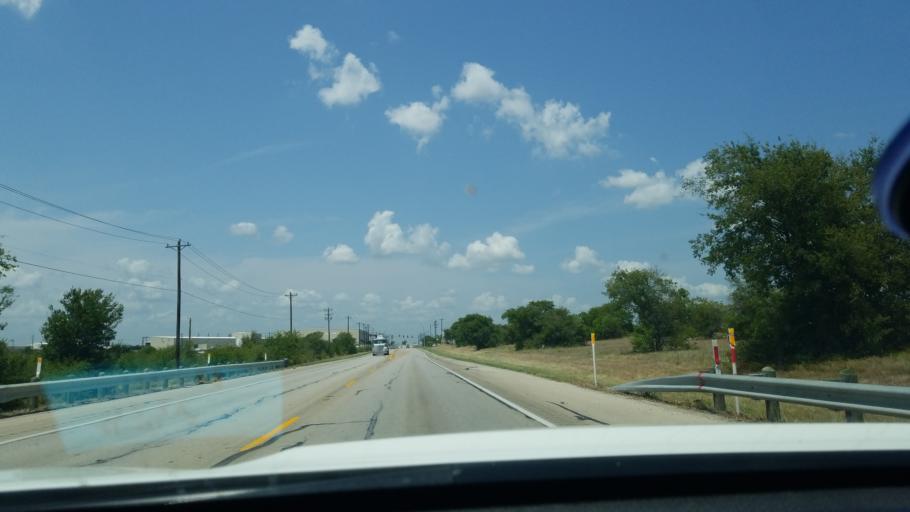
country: US
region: Texas
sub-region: Tarrant County
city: Eagle Mountain
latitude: 32.9318
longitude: -97.4159
